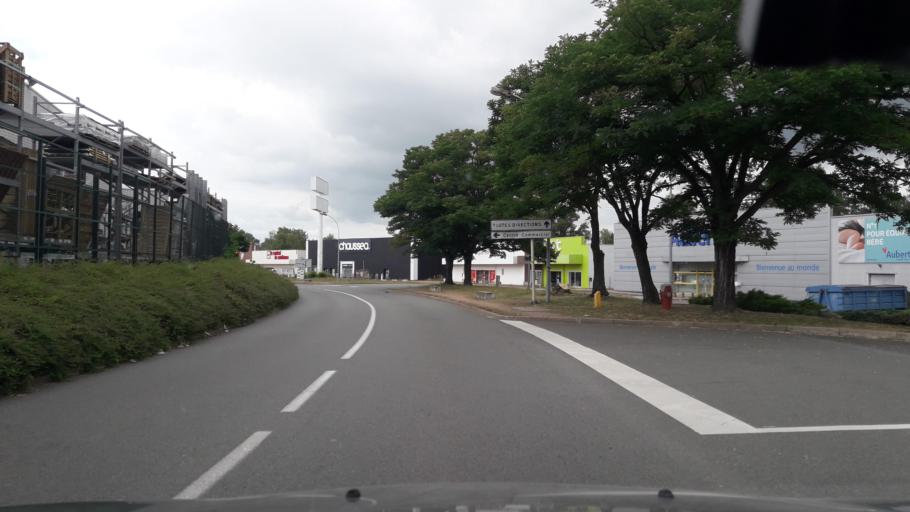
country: FR
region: Rhone-Alpes
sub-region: Departement de la Loire
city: Mably
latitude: 46.0672
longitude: 4.0612
